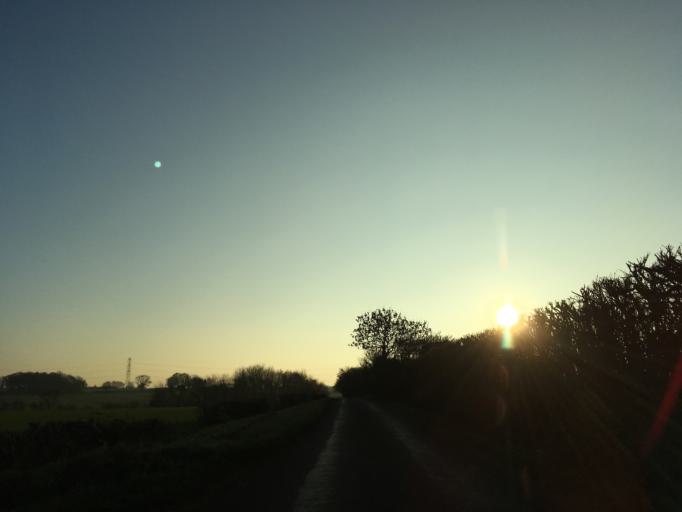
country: GB
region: England
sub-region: Wiltshire
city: Nettleton
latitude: 51.4854
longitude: -2.2613
